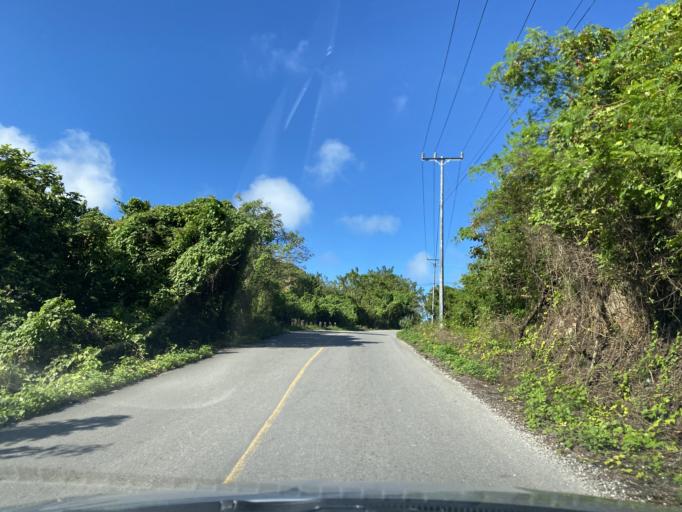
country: DO
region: Samana
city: Sanchez
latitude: 19.2476
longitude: -69.5956
